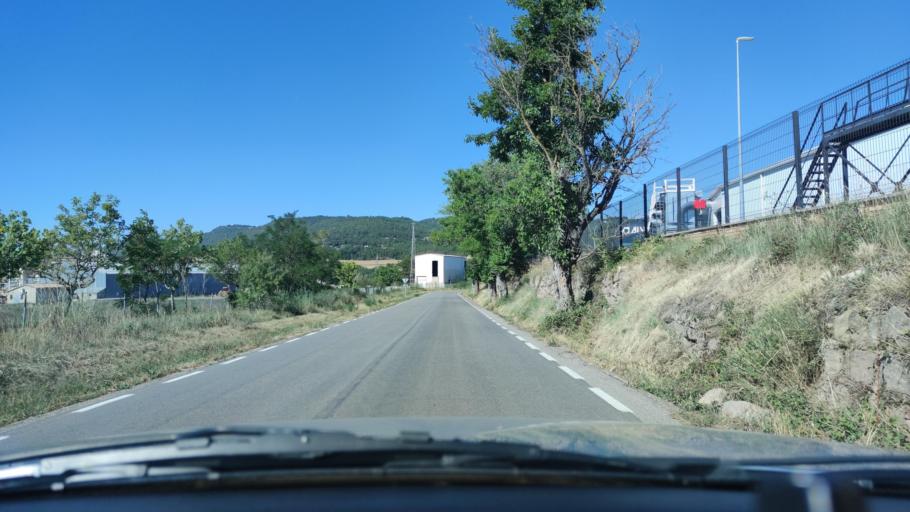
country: ES
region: Catalonia
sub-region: Provincia de Lleida
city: Solsona
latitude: 41.9892
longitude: 1.5104
